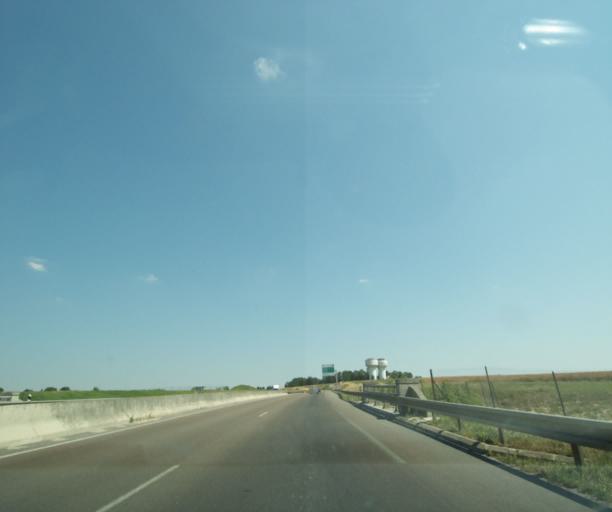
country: FR
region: Champagne-Ardenne
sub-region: Departement de la Marne
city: Saint-Memmie
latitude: 48.9582
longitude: 4.3899
